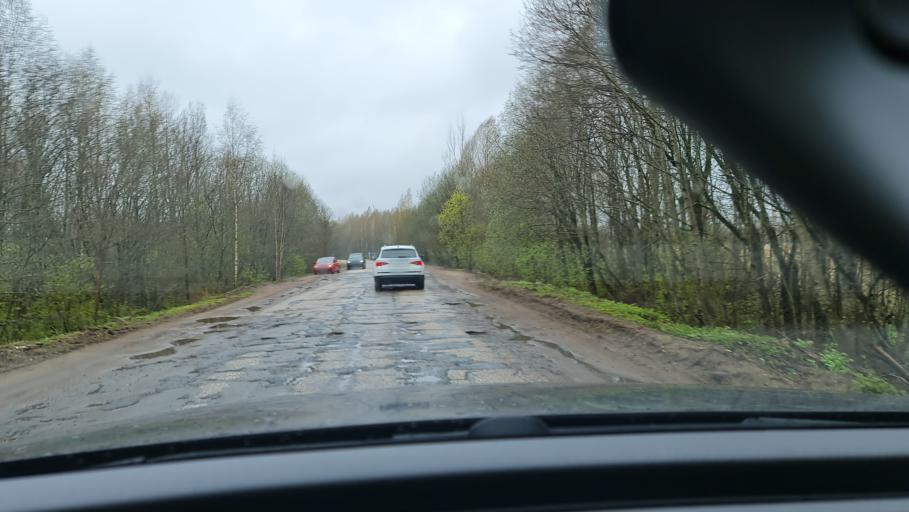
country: RU
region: Novgorod
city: Kresttsy
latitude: 57.9684
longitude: 32.7144
